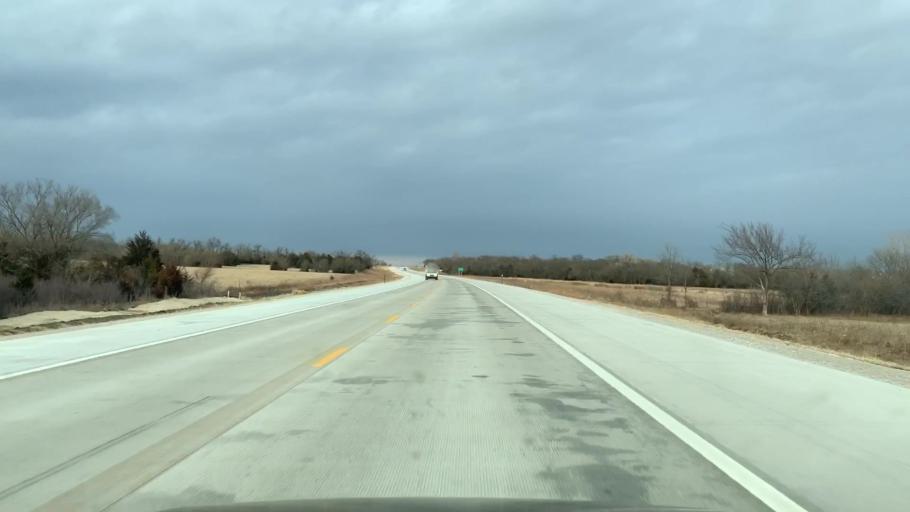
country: US
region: Kansas
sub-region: Allen County
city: Iola
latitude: 37.8632
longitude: -95.4039
